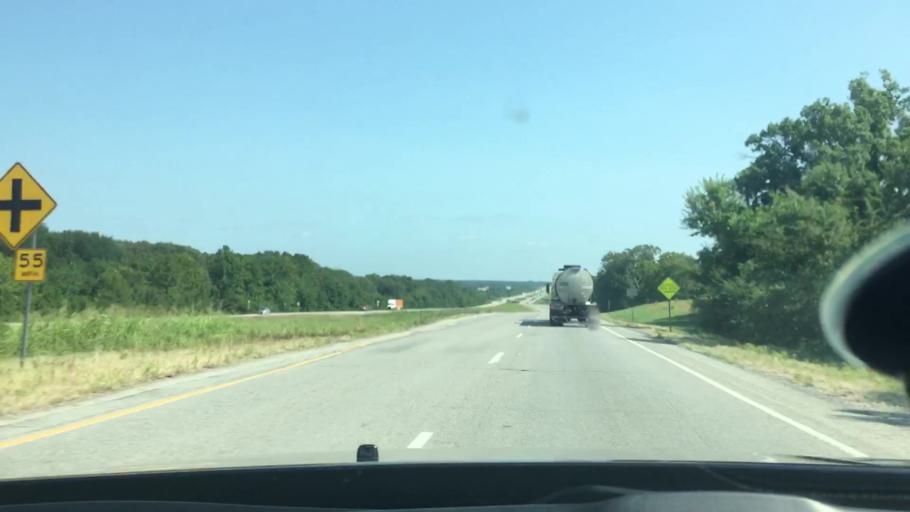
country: US
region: Oklahoma
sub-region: Atoka County
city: Atoka
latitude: 34.2326
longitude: -96.2224
